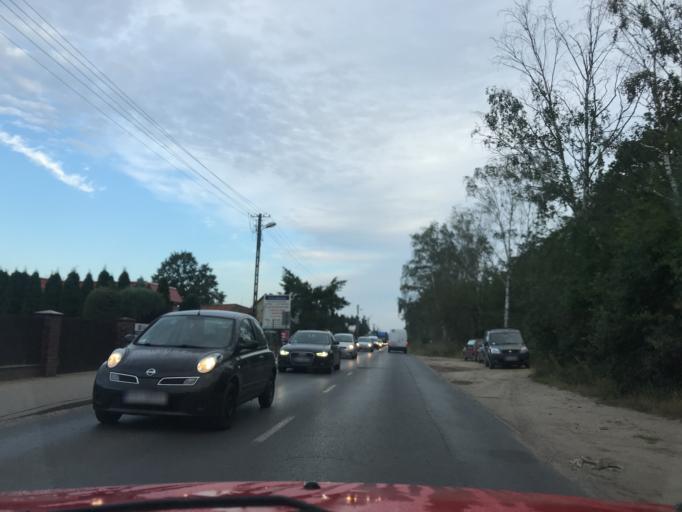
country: PL
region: Greater Poland Voivodeship
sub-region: Powiat poznanski
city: Plewiska
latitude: 52.3996
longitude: 16.8004
